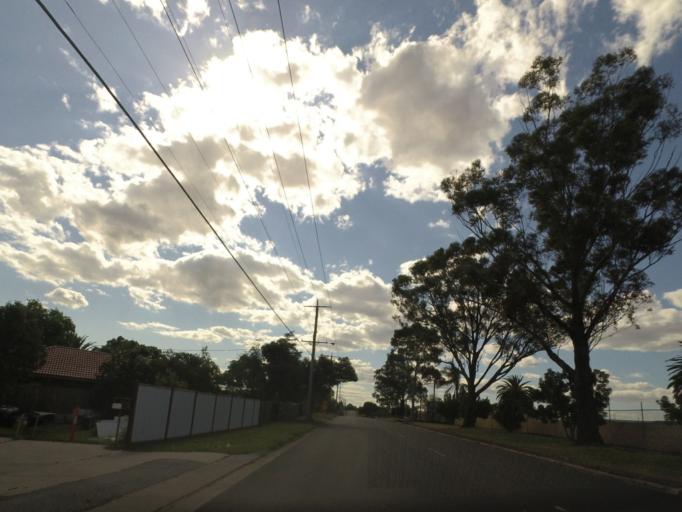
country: AU
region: Victoria
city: Heatherton
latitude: -37.9714
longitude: 145.1178
